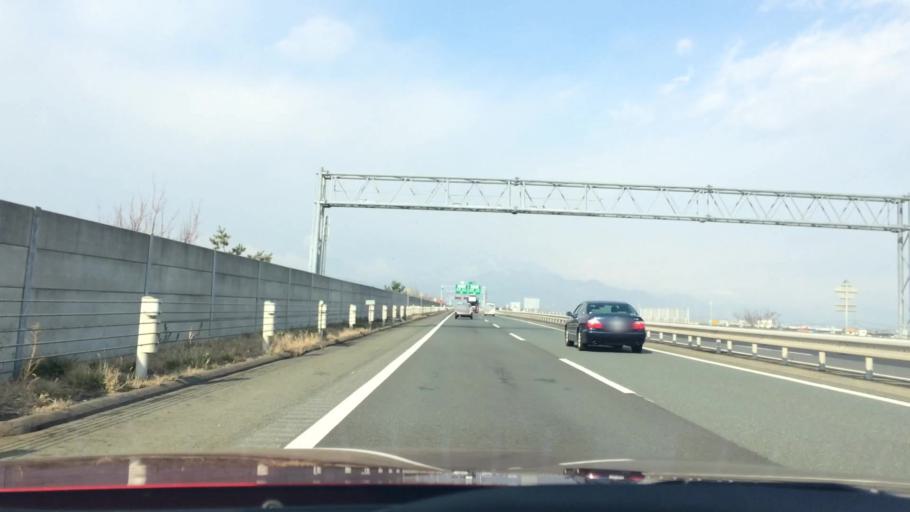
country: JP
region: Nagano
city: Nagano-shi
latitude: 36.5395
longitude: 138.1396
